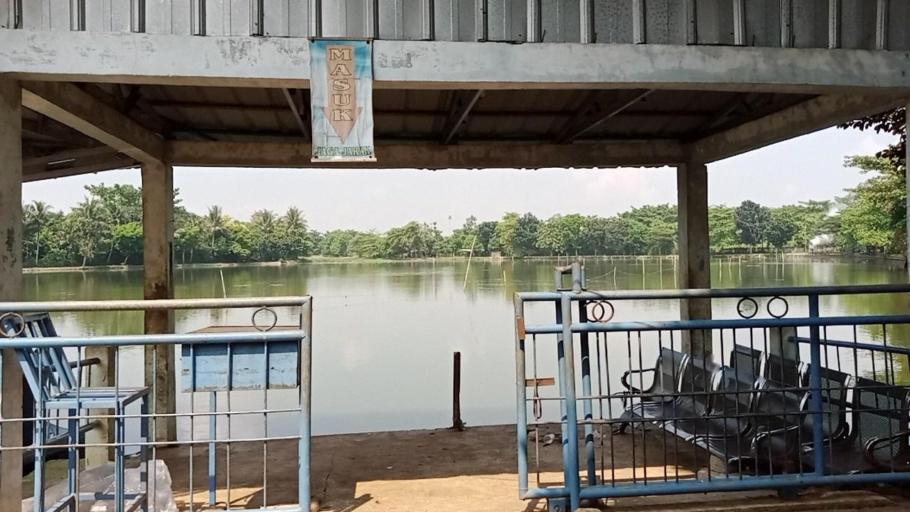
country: ID
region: West Java
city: Parung
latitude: -6.4205
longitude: 106.7499
